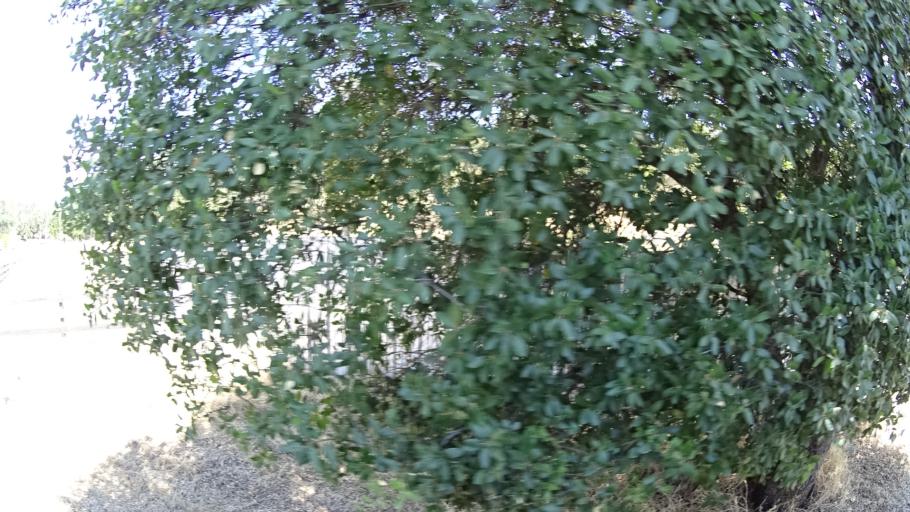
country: US
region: California
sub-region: Calaveras County
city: Angels Camp
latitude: 38.0871
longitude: -120.5559
